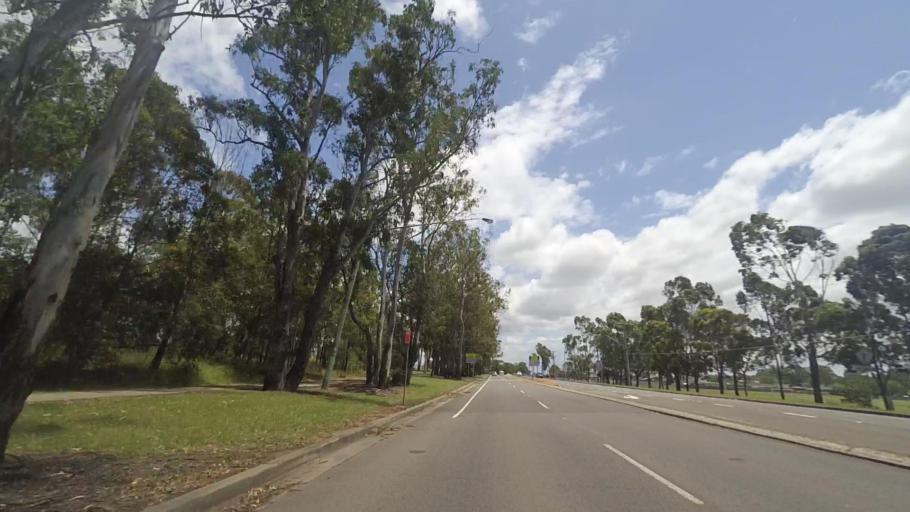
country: AU
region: New South Wales
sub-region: Liverpool
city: Holsworthy
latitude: -33.9552
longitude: 150.9550
